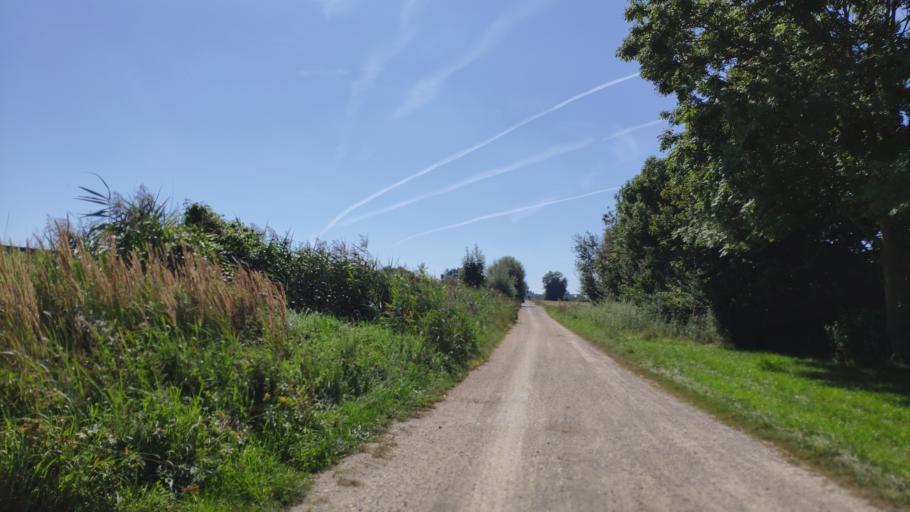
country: DE
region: Bavaria
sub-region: Swabia
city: Neu-Ulm
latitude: 48.3660
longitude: 10.0329
